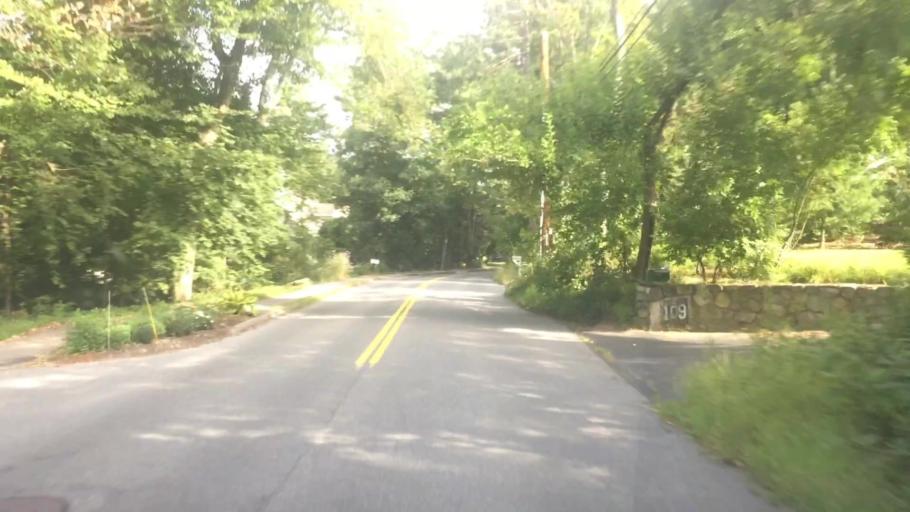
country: US
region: Massachusetts
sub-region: Middlesex County
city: Acton
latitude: 42.4707
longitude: -71.4585
